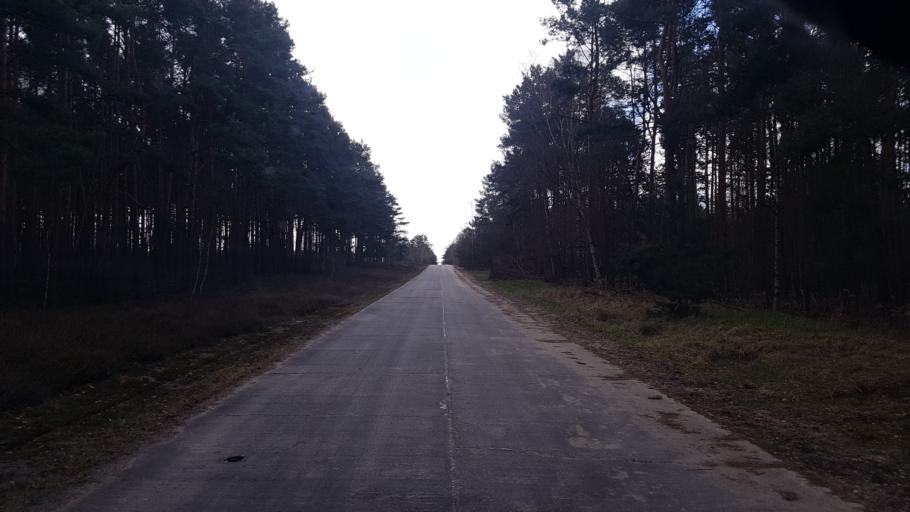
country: DE
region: Brandenburg
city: Schonborn
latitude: 51.6382
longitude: 13.5074
